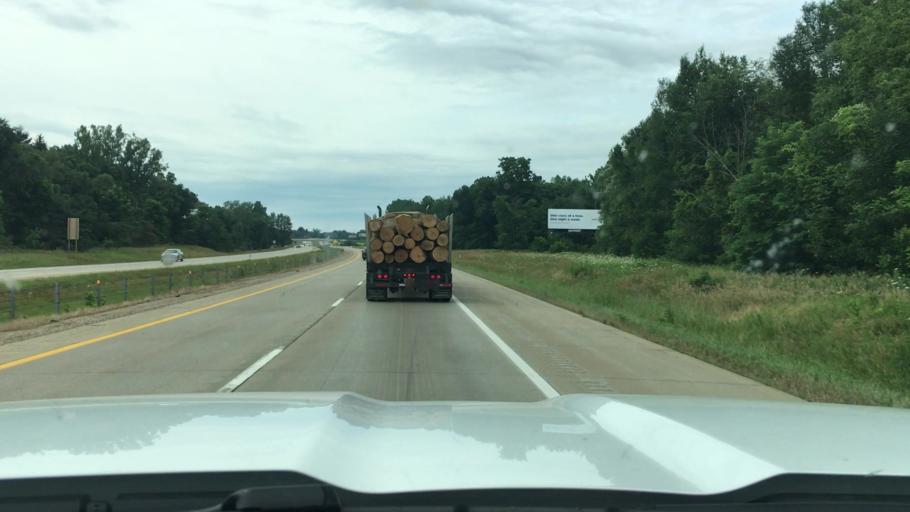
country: US
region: Michigan
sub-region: Allegan County
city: Plainwell
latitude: 42.4736
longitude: -85.6532
